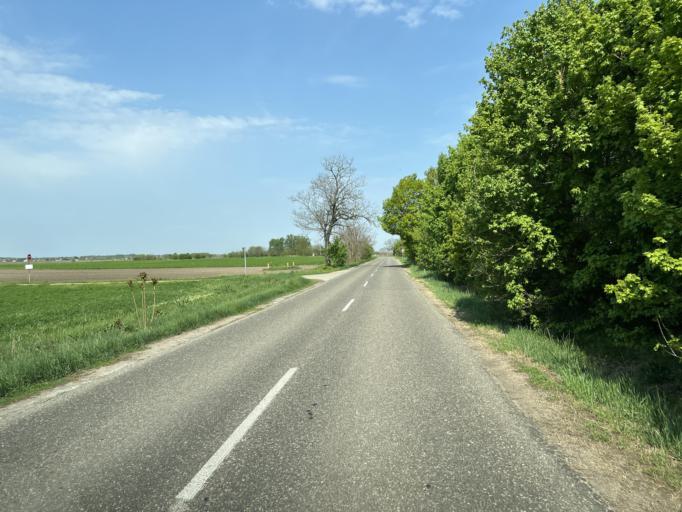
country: HU
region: Pest
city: Tortel
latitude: 47.1140
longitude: 19.9727
